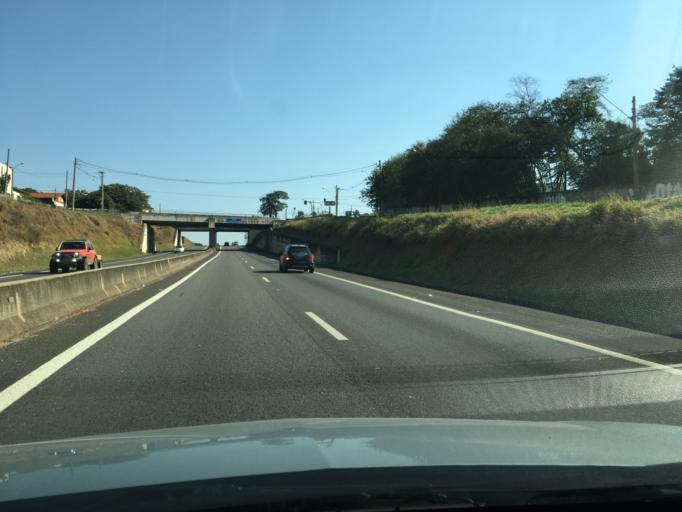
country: BR
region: Sao Paulo
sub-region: Sao Joao Da Boa Vista
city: Sao Joao da Boa Vista
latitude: -21.9840
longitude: -46.7878
